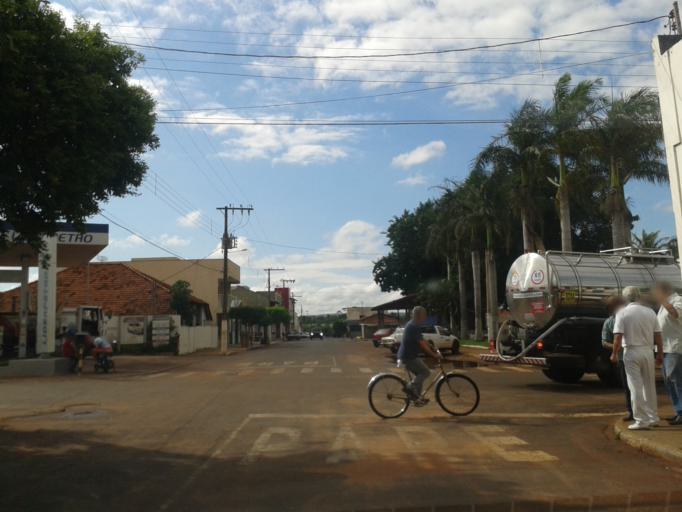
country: BR
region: Minas Gerais
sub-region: Ituiutaba
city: Ituiutaba
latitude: -19.2136
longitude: -49.7869
